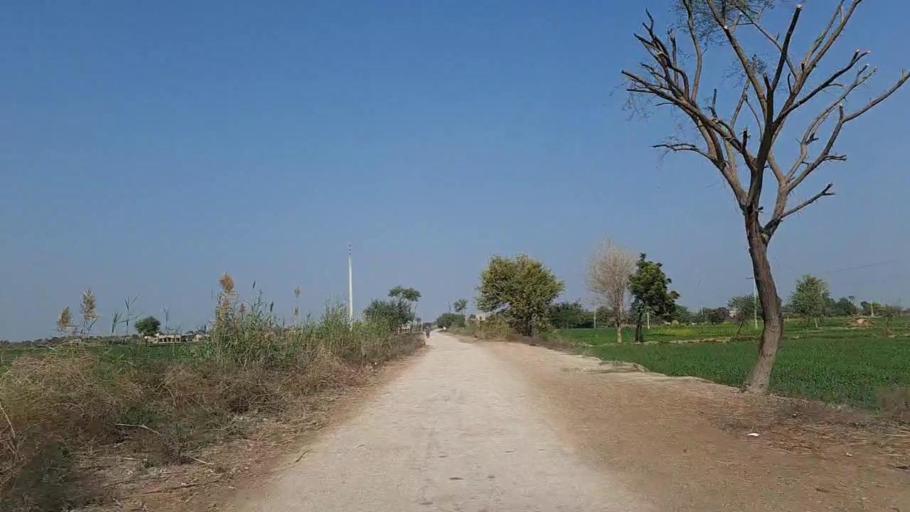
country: PK
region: Sindh
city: Nawabshah
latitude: 26.2843
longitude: 68.5137
